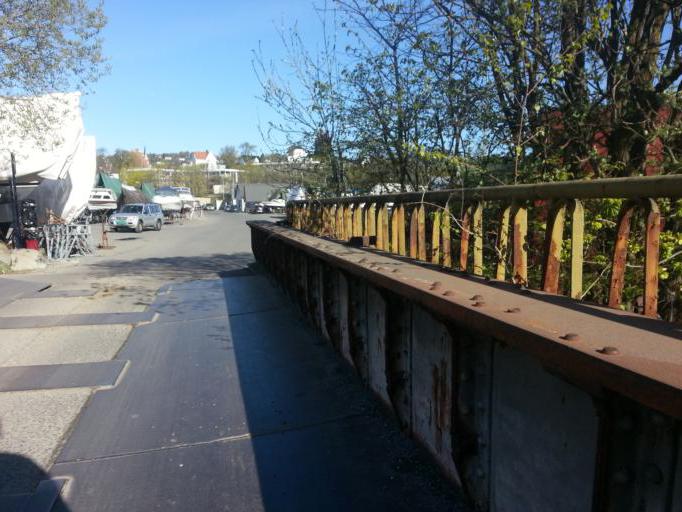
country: NO
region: Oslo
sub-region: Oslo
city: Sjolyststranda
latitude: 59.9193
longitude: 10.6765
